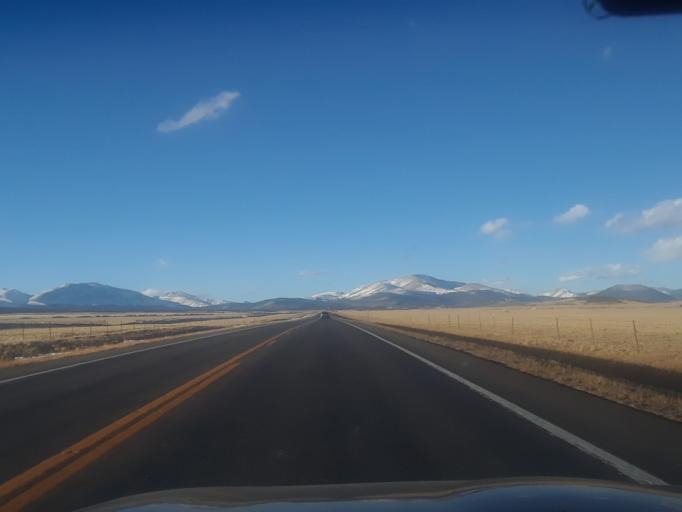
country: US
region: Colorado
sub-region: Park County
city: Fairplay
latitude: 39.1423
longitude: -105.9971
